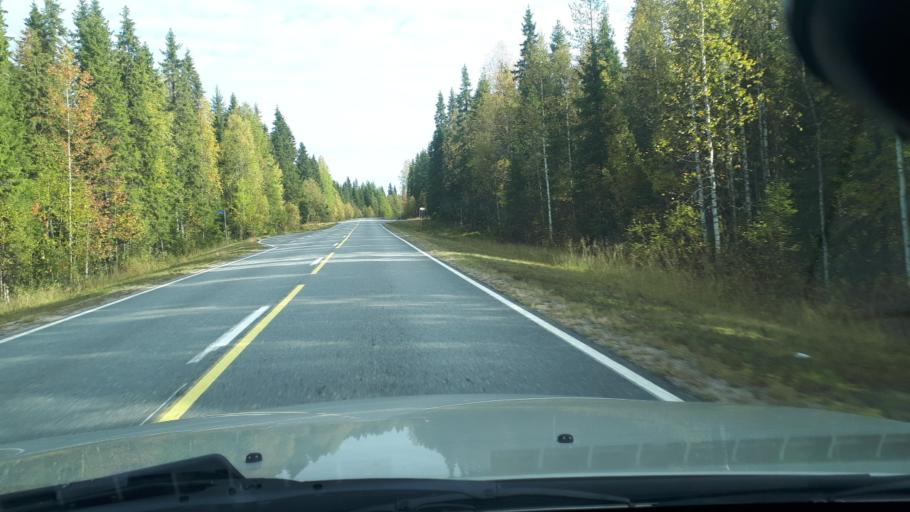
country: FI
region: Northern Ostrobothnia
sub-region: Oulu
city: Yli-Ii
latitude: 65.9491
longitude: 25.9070
